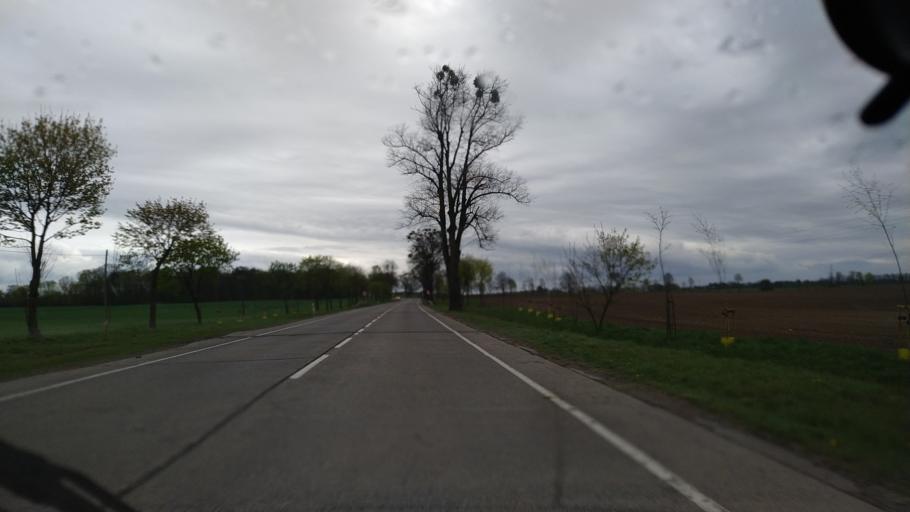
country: PL
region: Pomeranian Voivodeship
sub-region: Powiat starogardzki
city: Zblewo
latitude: 53.9317
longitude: 18.3660
